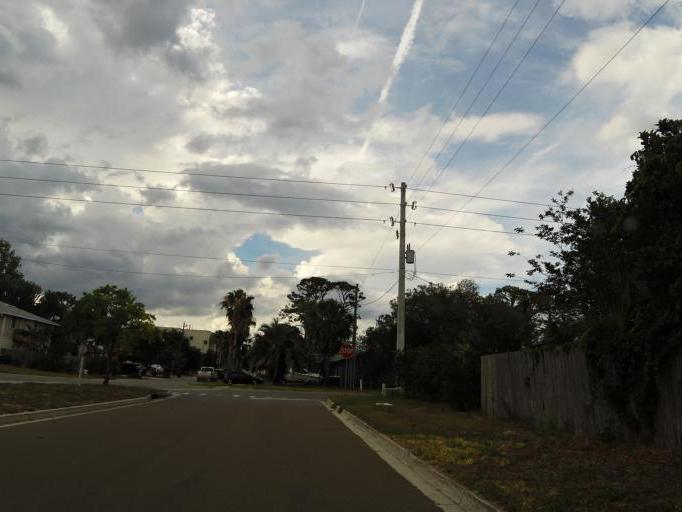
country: US
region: Florida
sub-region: Duval County
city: Jacksonville Beach
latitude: 30.2706
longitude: -81.3990
